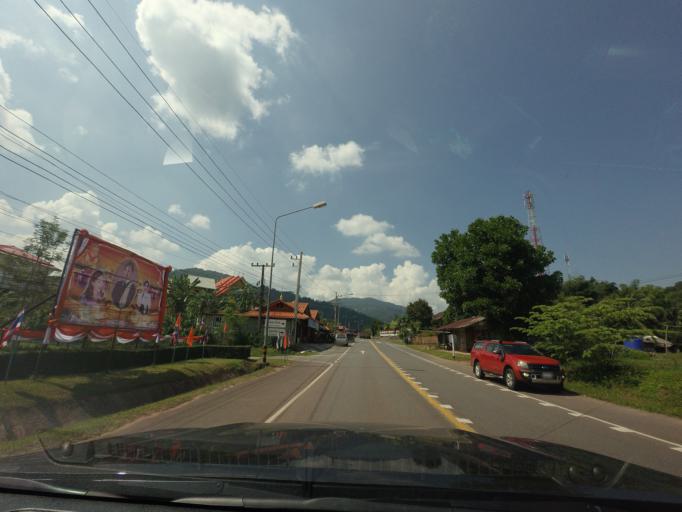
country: TH
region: Nan
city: Bo Kluea
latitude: 19.0808
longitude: 101.1542
